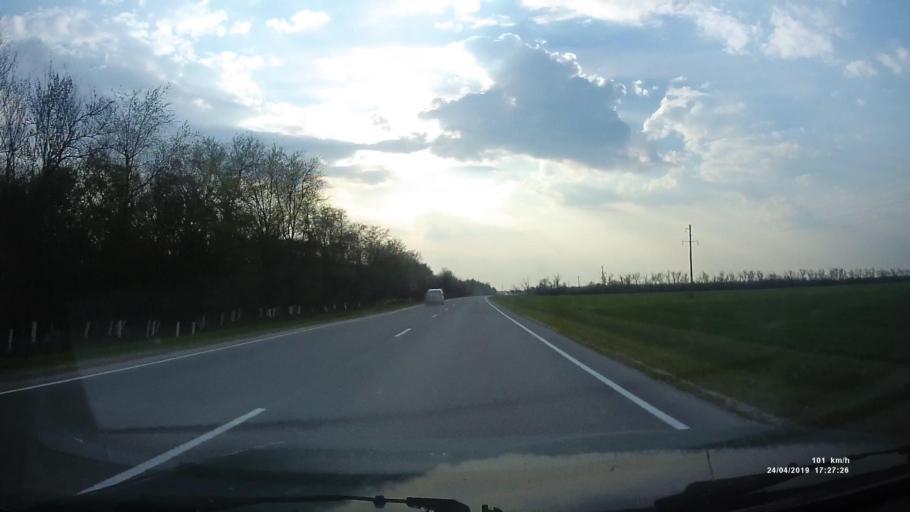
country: RU
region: Rostov
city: Gigant
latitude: 46.5280
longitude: 41.1993
